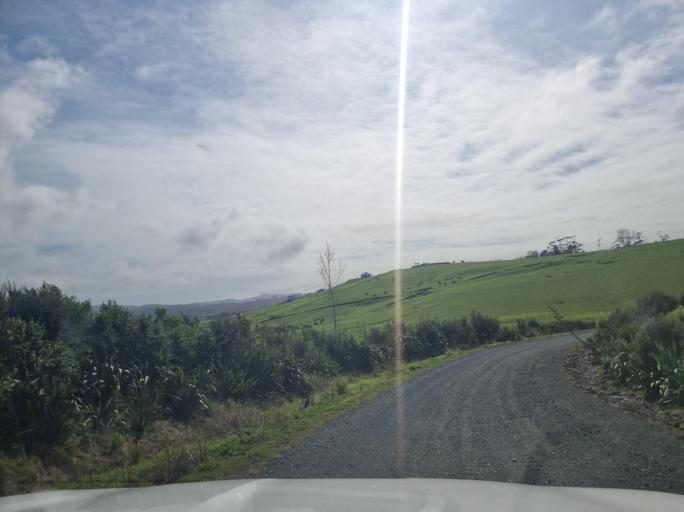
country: NZ
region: Auckland
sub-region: Auckland
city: Wellsford
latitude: -36.1385
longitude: 174.4938
